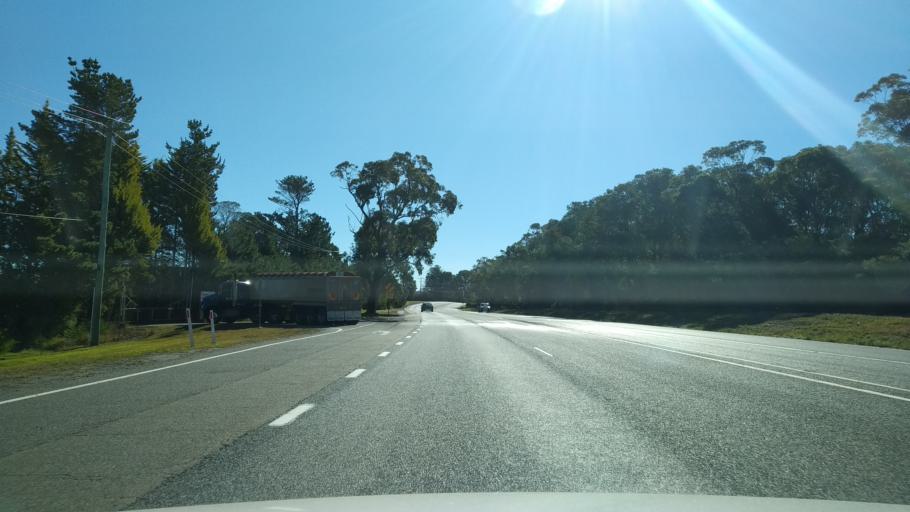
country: AU
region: New South Wales
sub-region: Gosford Shire
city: Point Clare
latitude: -33.4114
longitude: 151.2191
